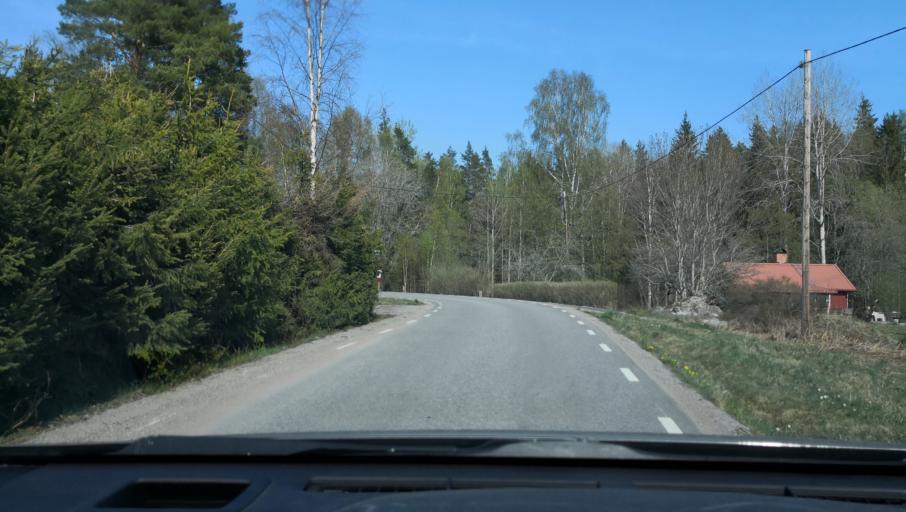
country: SE
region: Vaestmanland
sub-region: Sala Kommun
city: Sala
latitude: 60.0060
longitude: 16.6745
